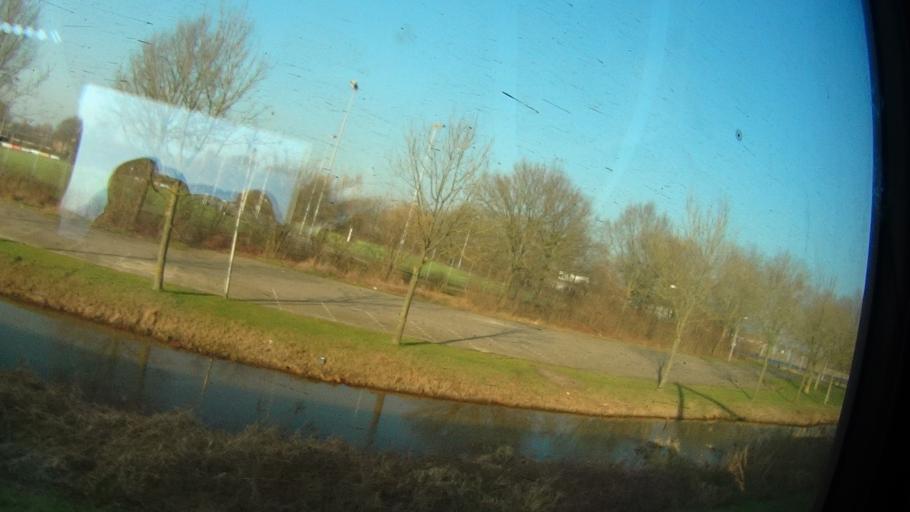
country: NL
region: Overijssel
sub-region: Gemeente Zwolle
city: Zwolle
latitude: 52.4985
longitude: 6.1213
